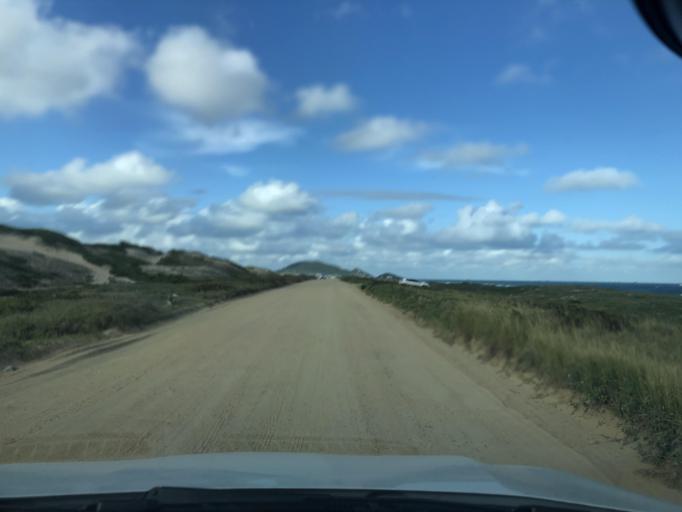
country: BR
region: Santa Catarina
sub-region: Sao Francisco Do Sul
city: Sao Francisco do Sul
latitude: -26.2522
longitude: -48.5141
